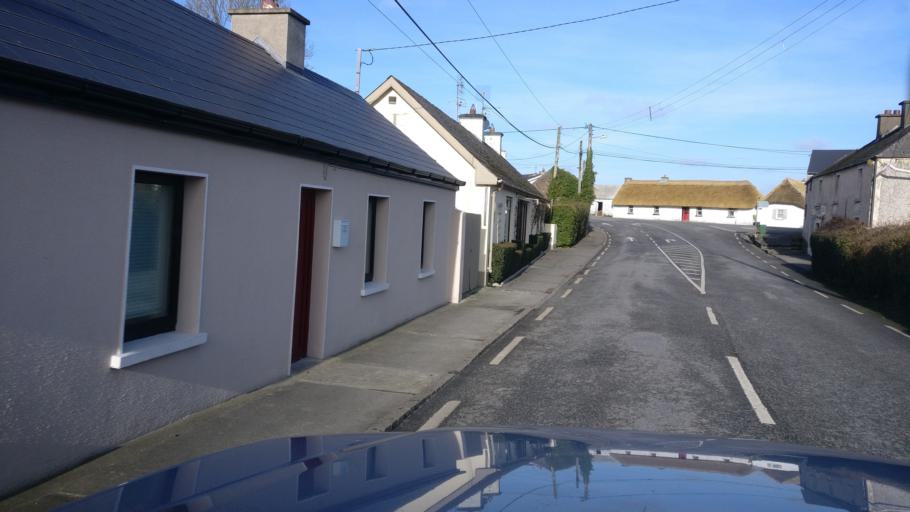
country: IE
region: Leinster
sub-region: Kilkenny
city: Castlecomer
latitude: 52.8597
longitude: -7.1635
